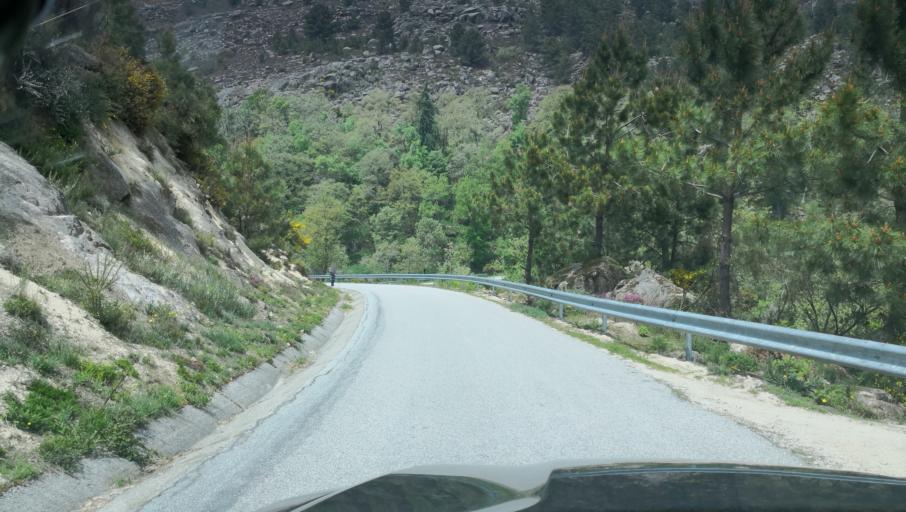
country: PT
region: Vila Real
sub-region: Vila Real
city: Vila Real
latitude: 41.3189
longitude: -7.7955
